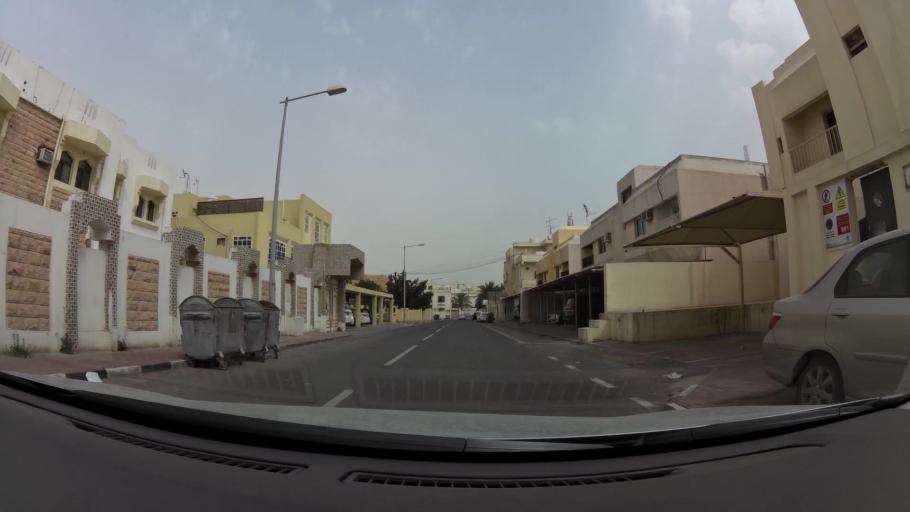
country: QA
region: Baladiyat ad Dawhah
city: Doha
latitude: 25.2597
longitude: 51.5274
